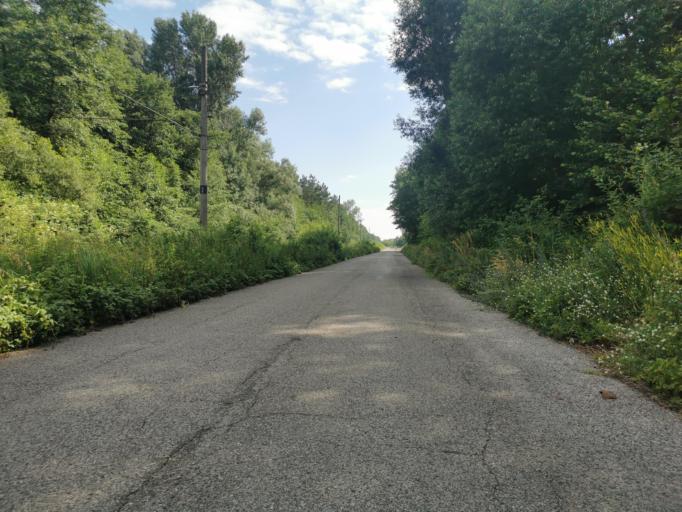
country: SK
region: Trnavsky
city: Gbely
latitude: 48.7168
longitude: 17.0866
